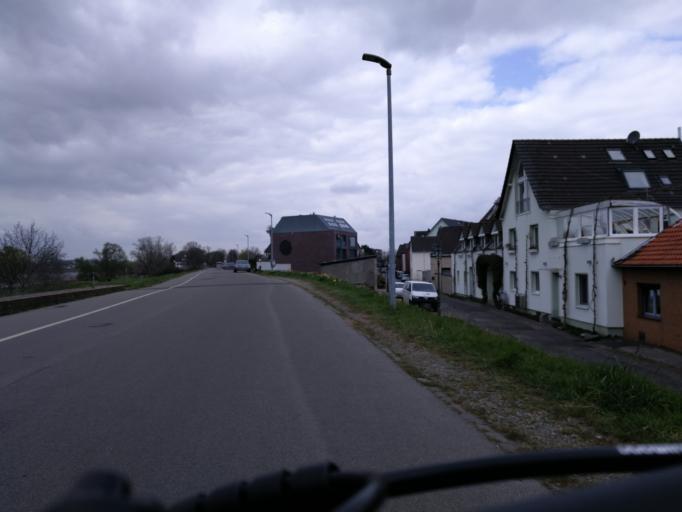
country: DE
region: North Rhine-Westphalia
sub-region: Regierungsbezirk Dusseldorf
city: Dusseldorf
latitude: 51.1846
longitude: 6.7630
